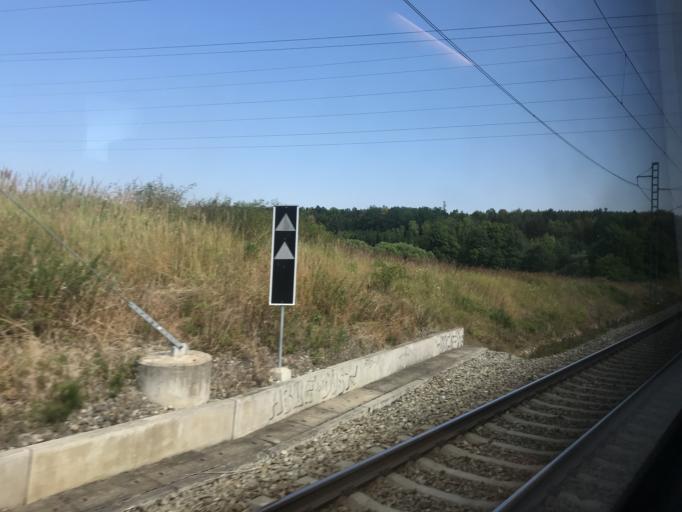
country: CZ
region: Central Bohemia
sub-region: Okres Benesov
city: Benesov
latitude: 49.7972
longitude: 14.7015
